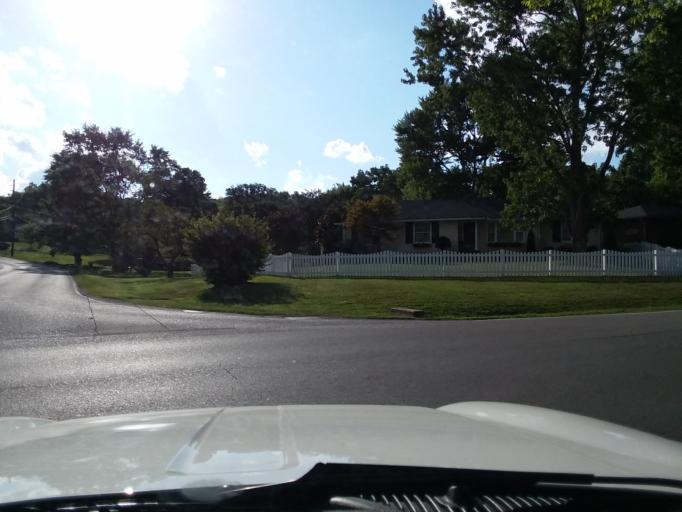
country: US
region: Tennessee
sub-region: Williamson County
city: Brentwood
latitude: 36.0599
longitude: -86.7591
